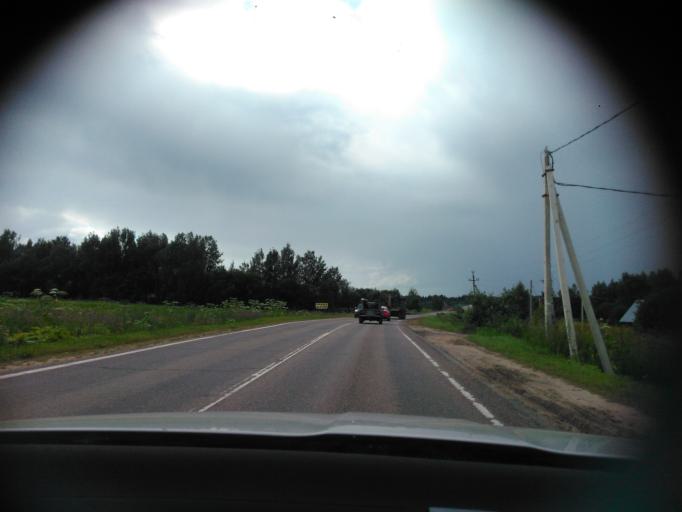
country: RU
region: Moskovskaya
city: Klin
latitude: 56.1560
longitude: 36.7484
